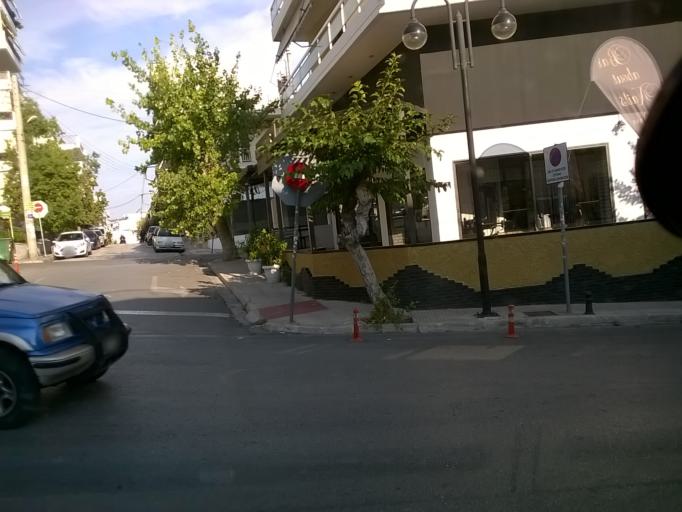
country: GR
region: Attica
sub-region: Nomarchia Athinas
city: Agios Dimitrios
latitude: 37.9283
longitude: 23.7352
